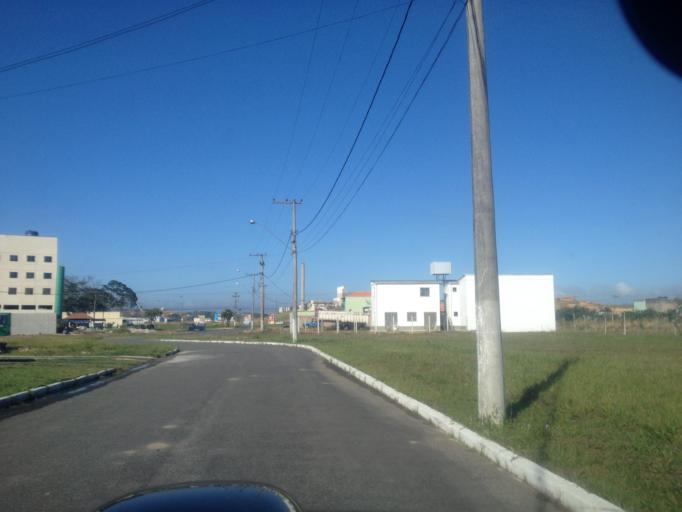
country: BR
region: Rio de Janeiro
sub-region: Porto Real
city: Porto Real
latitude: -22.4159
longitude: -44.3028
